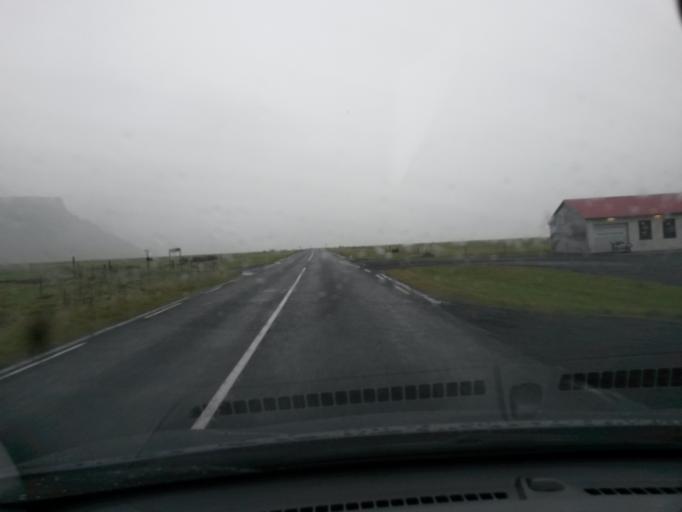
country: IS
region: South
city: Vestmannaeyjar
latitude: 63.5433
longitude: -19.6686
